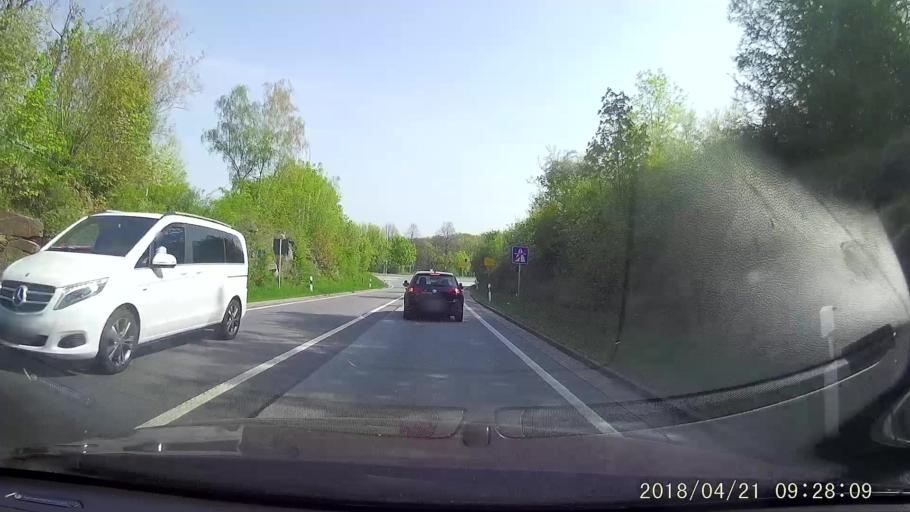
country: DE
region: Saxony
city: Bautzen
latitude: 51.1899
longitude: 14.4118
